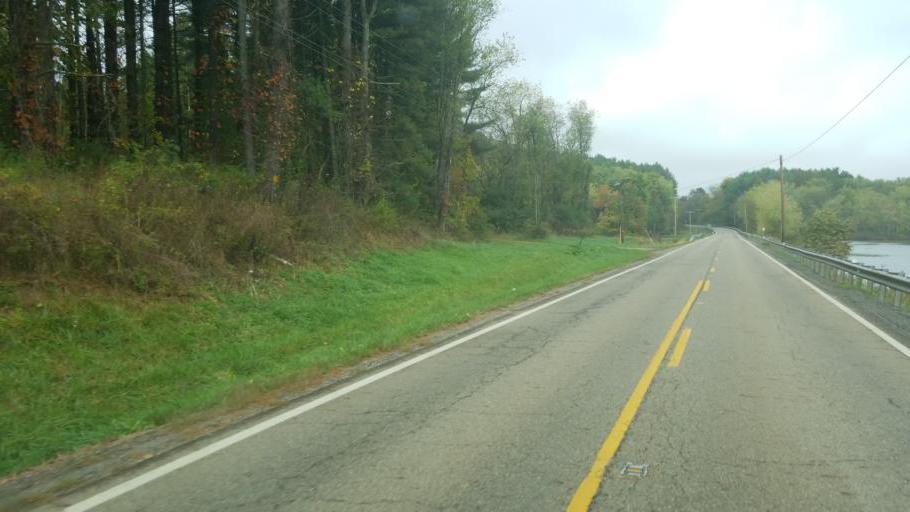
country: US
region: Ohio
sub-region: Tuscarawas County
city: Rockford
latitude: 40.5605
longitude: -81.2552
